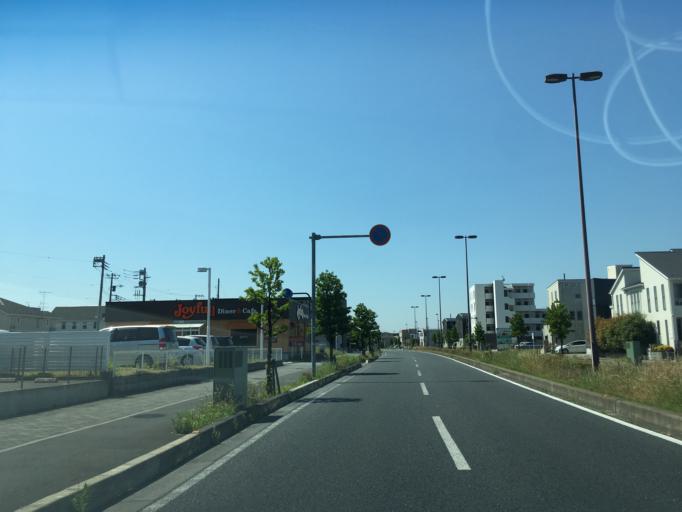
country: JP
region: Saitama
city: Yoshikawa
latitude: 35.8835
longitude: 139.8154
